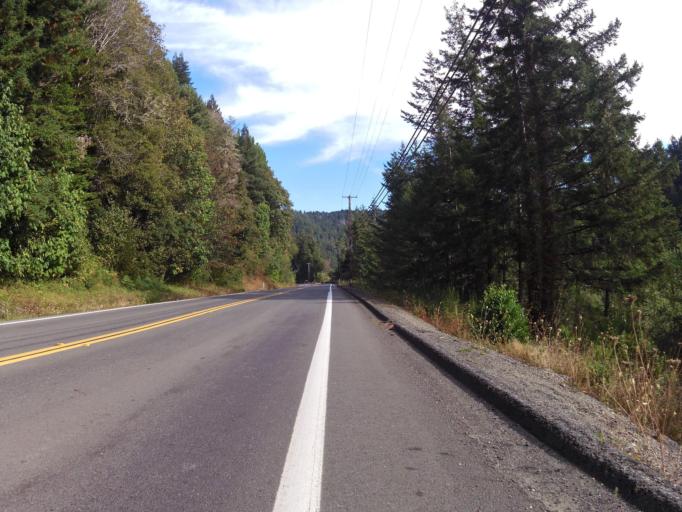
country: US
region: California
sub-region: Del Norte County
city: Bertsch-Oceanview
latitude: 41.8158
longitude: -124.0894
